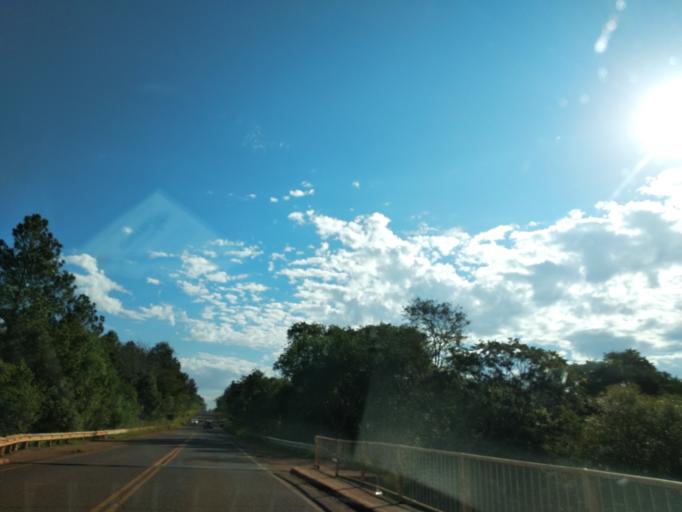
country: AR
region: Misiones
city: Ruiz de Montoya
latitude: -27.0590
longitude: -55.0129
